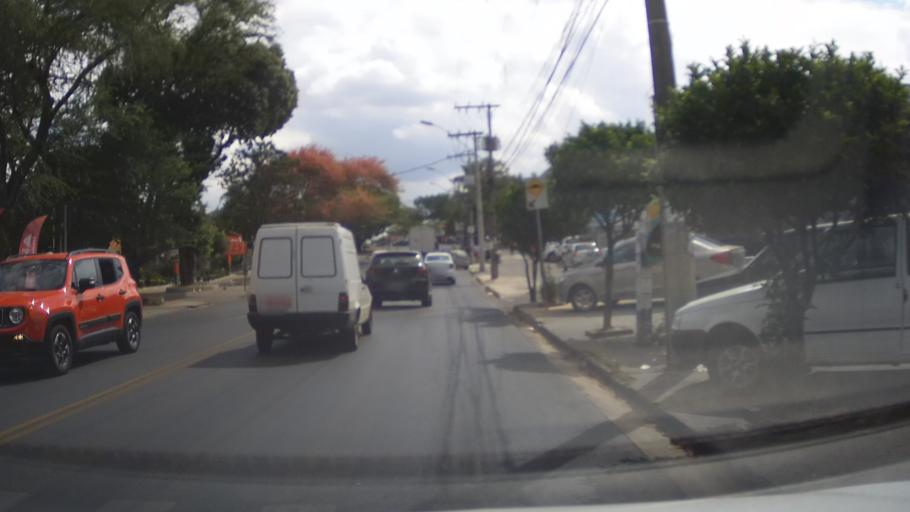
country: BR
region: Minas Gerais
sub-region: Belo Horizonte
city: Belo Horizonte
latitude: -19.8457
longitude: -43.9726
